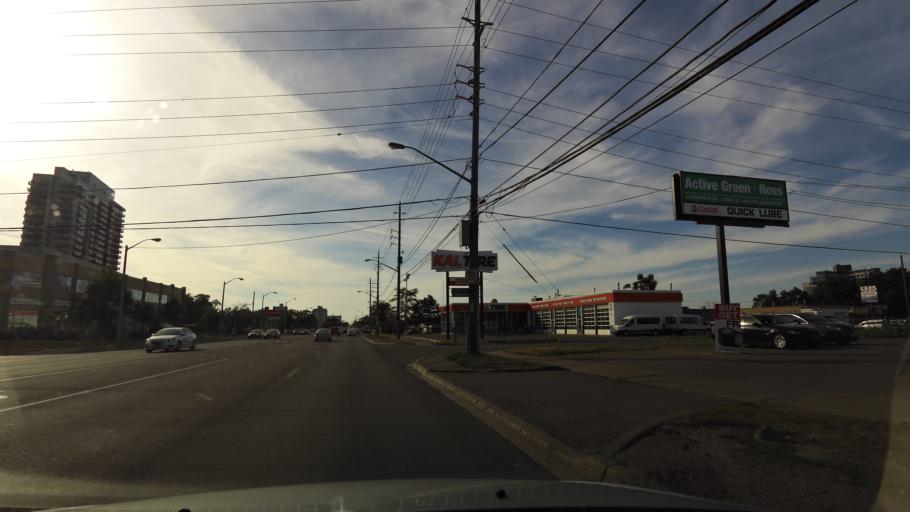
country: CA
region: Ontario
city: Brampton
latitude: 43.6938
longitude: -79.7468
